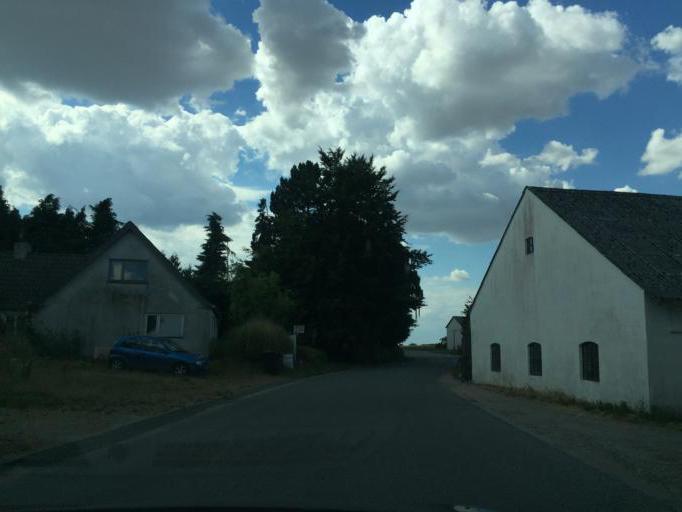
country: DK
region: South Denmark
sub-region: Assens Kommune
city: Harby
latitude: 55.2148
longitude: 10.0555
